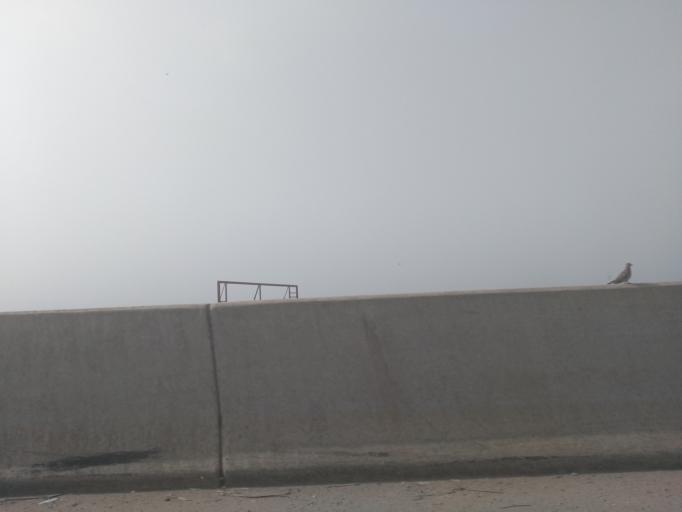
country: GH
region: Greater Accra
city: Gbawe
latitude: 5.5697
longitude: -0.2832
